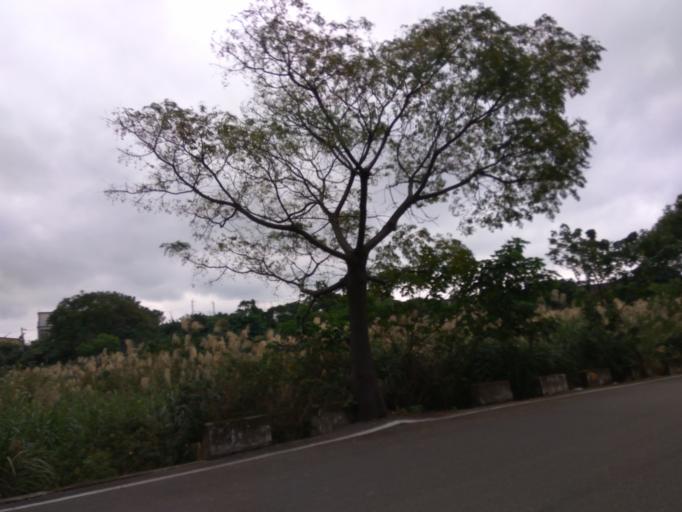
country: TW
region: Taiwan
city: Taoyuan City
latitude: 25.0242
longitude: 121.2242
